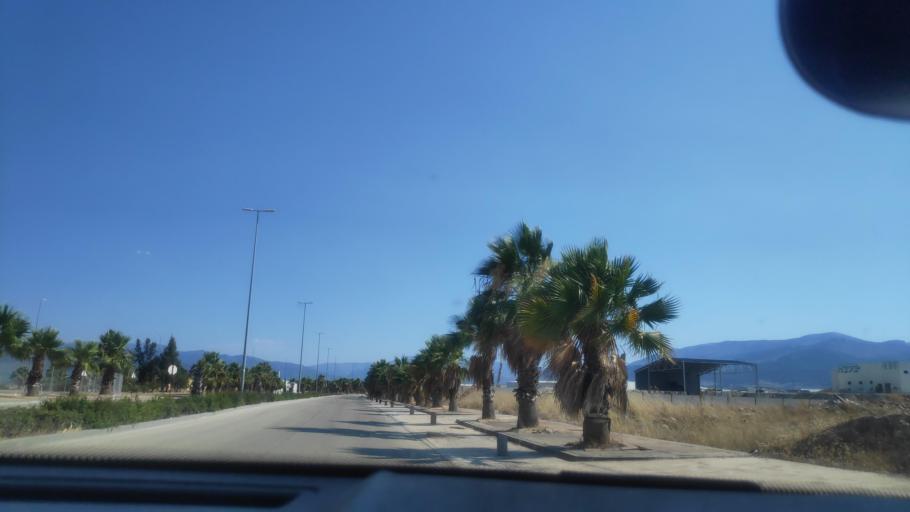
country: ES
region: Andalusia
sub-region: Provincia de Jaen
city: Jaen
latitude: 37.8248
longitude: -3.7761
